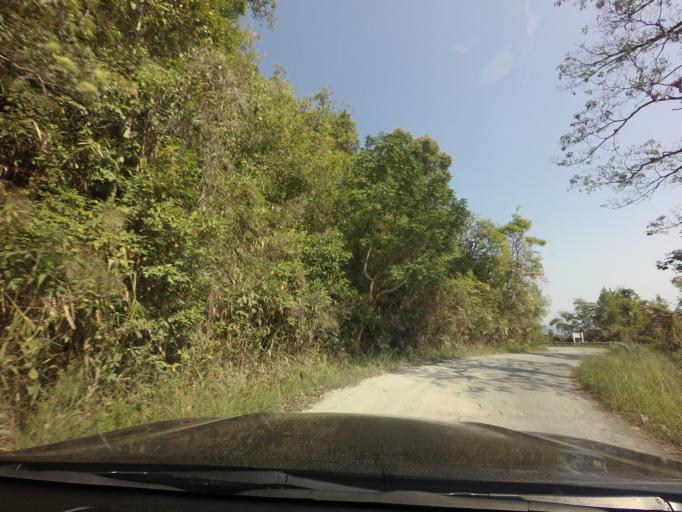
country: TH
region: Kanchanaburi
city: Thong Pha Phum
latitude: 14.6915
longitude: 98.4573
